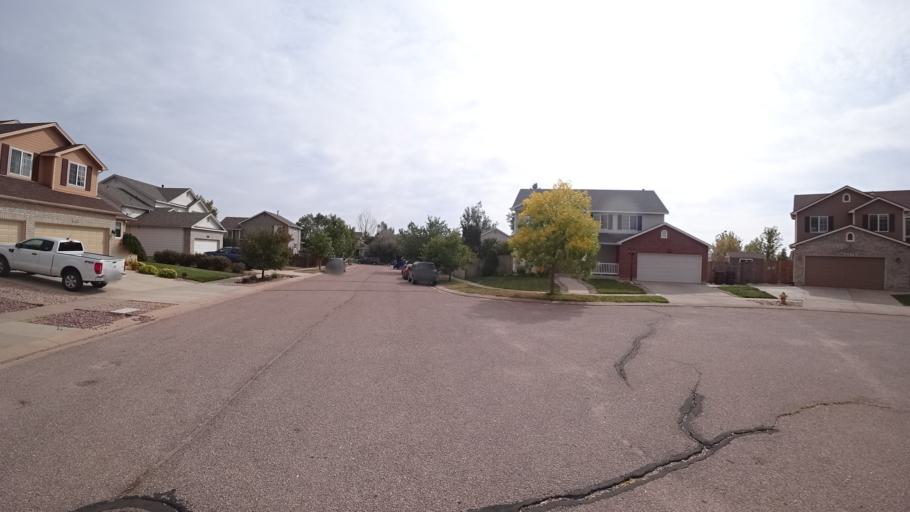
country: US
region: Colorado
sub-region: El Paso County
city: Cimarron Hills
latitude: 38.9161
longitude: -104.7087
